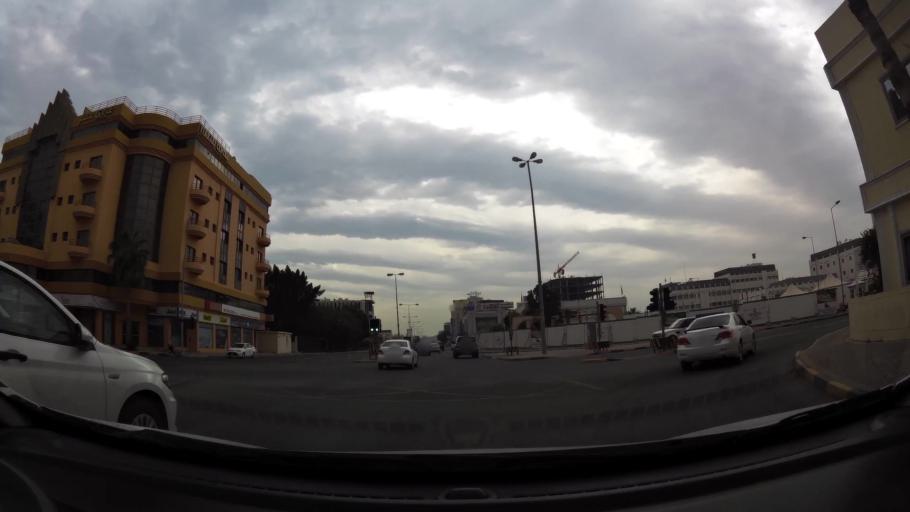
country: BH
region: Manama
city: Manama
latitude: 26.2152
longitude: 50.5892
